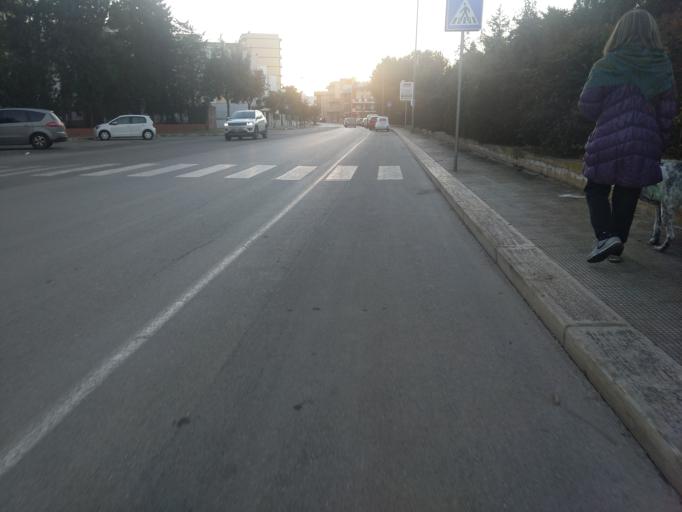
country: IT
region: Apulia
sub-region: Provincia di Bari
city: Modugno
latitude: 41.0790
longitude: 16.7881
